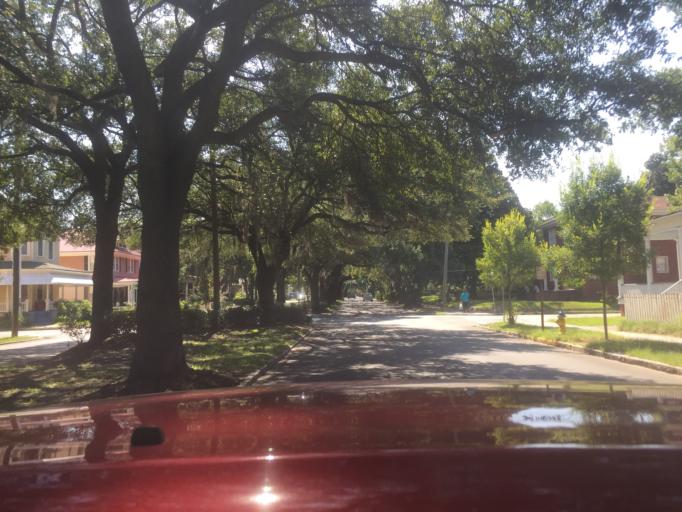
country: US
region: Georgia
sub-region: Chatham County
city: Savannah
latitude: 32.0581
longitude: -81.1040
